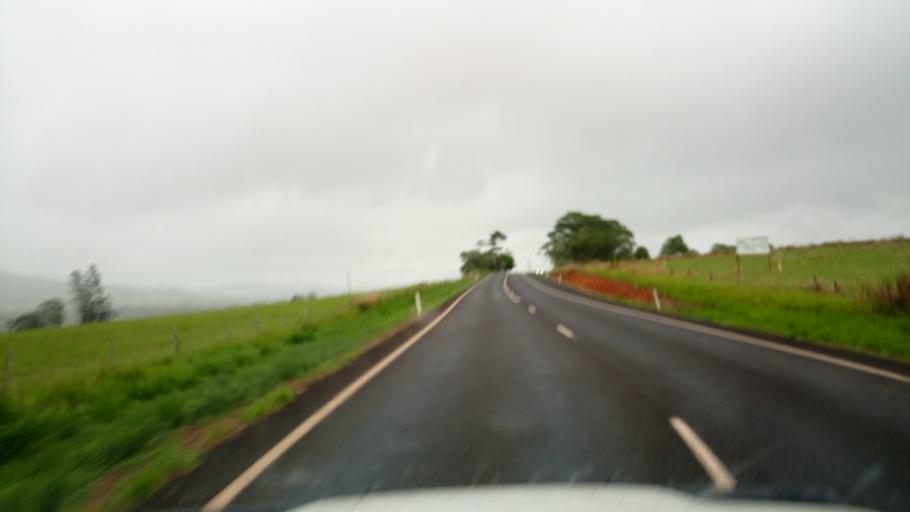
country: AU
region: Queensland
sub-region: Tablelands
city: Atherton
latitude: -17.2808
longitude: 145.5980
